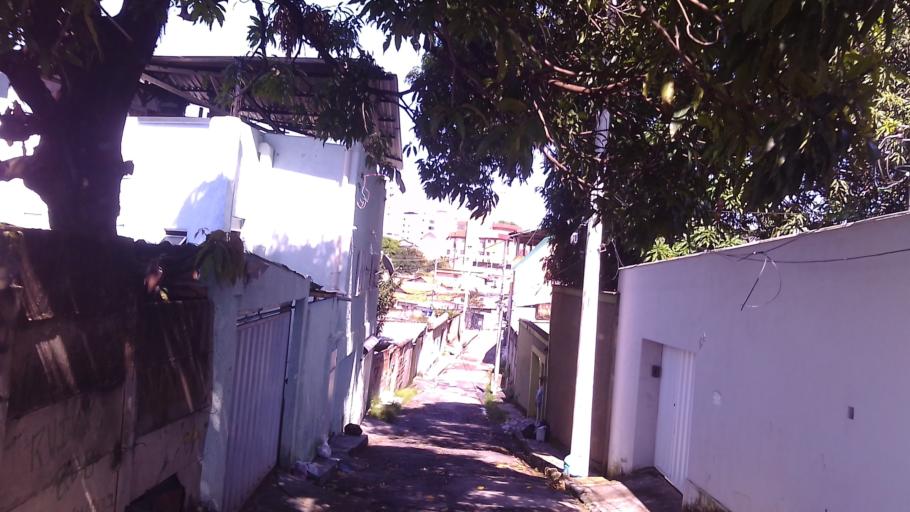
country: BR
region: Minas Gerais
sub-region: Belo Horizonte
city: Belo Horizonte
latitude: -19.9027
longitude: -43.9124
